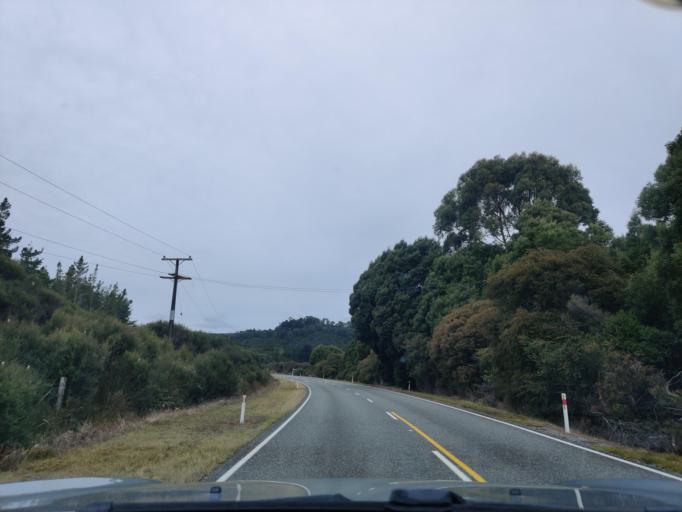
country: NZ
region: West Coast
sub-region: Buller District
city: Westport
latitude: -41.8941
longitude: 171.4587
